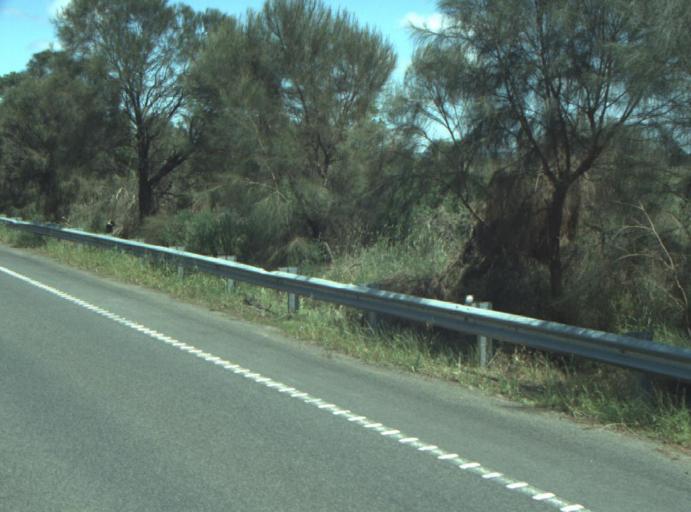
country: AU
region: Victoria
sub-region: Queenscliffe
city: Queenscliff
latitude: -38.1856
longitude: 144.6815
